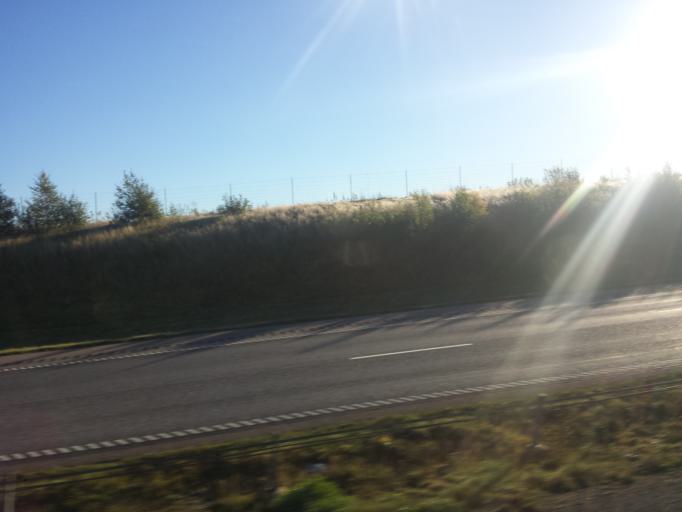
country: SE
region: Halland
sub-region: Halmstads Kommun
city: Getinge
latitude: 56.7749
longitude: 12.8079
